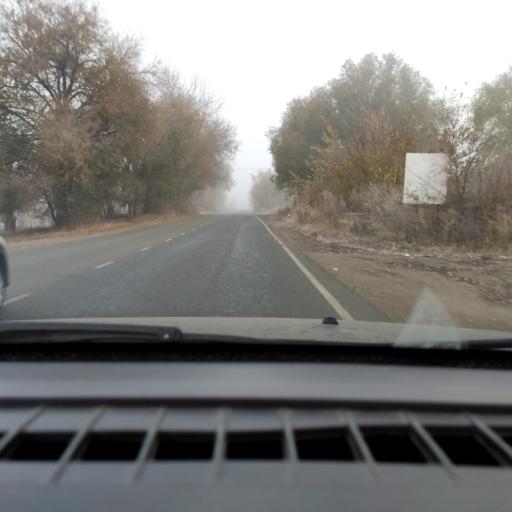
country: RU
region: Samara
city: Tol'yatti
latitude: 53.5832
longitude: 49.2567
